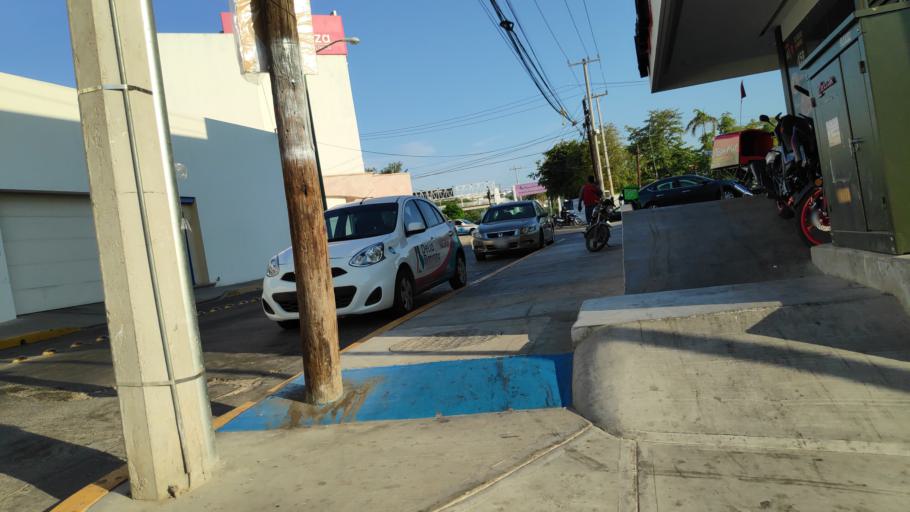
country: MX
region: Sinaloa
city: Culiacan
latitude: 24.7899
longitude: -107.3961
